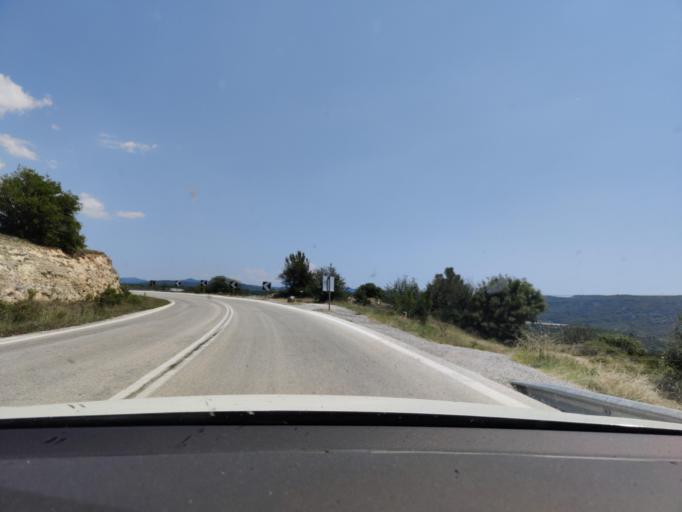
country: GR
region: East Macedonia and Thrace
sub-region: Nomos Kavalas
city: Paralia Ofryniou
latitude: 40.8049
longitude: 23.9674
